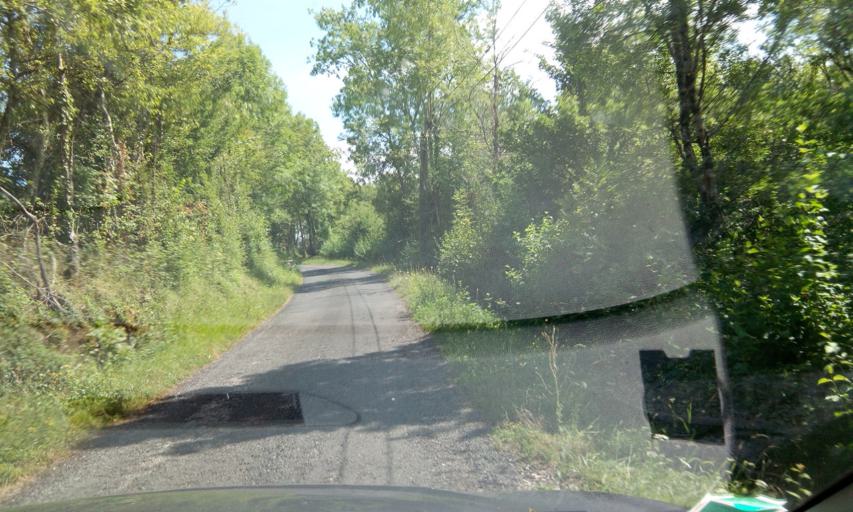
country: FR
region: Limousin
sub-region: Departement de la Correze
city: Cosnac
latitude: 45.0579
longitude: 1.5787
